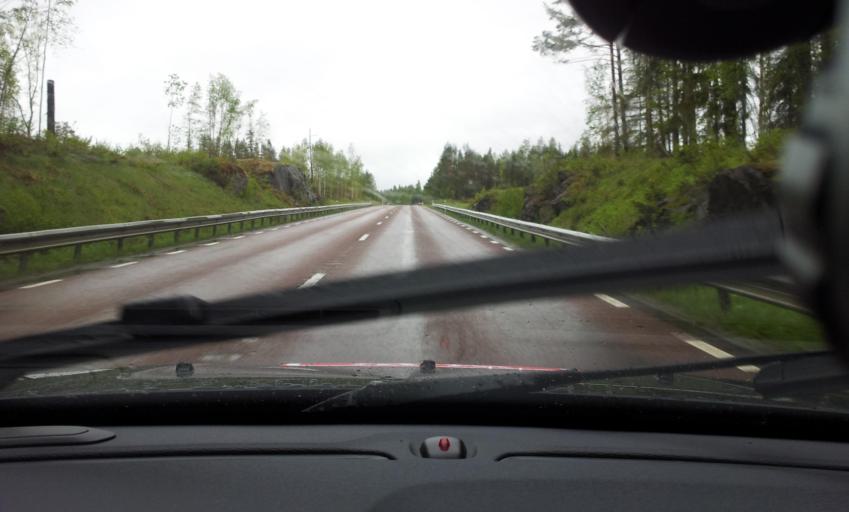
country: SE
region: Jaemtland
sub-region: Bergs Kommun
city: Hoverberg
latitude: 62.8868
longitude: 14.5237
